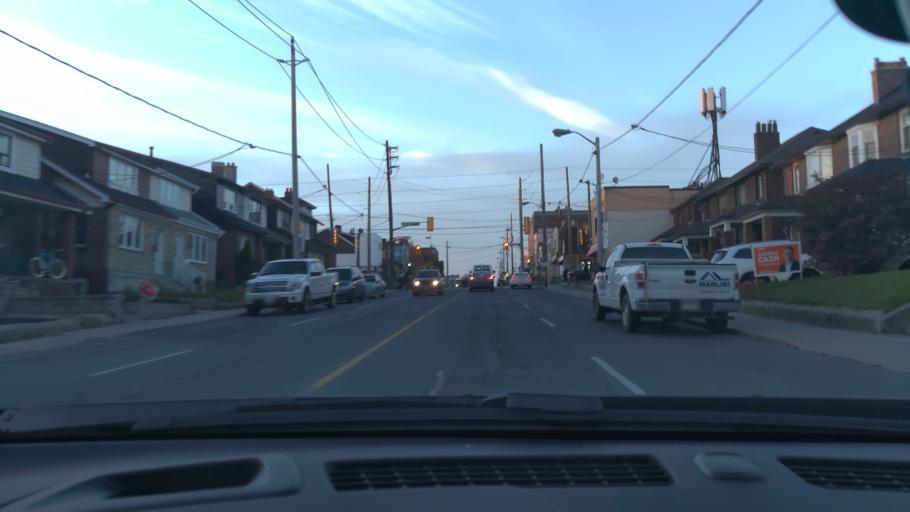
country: CA
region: Ontario
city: Toronto
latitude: 43.6849
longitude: -79.4458
